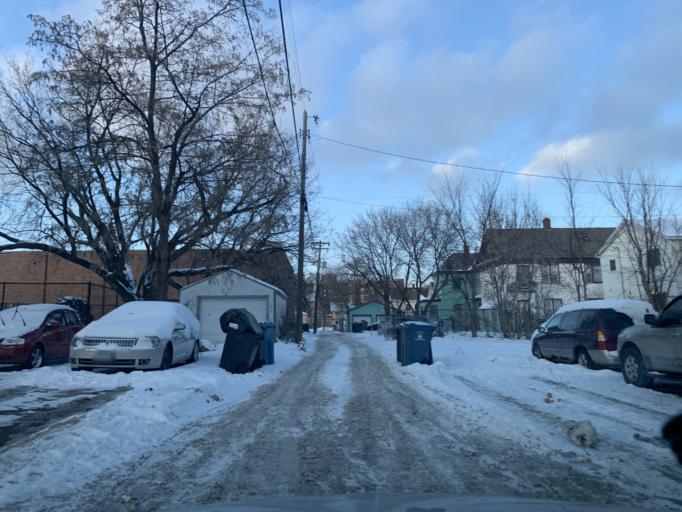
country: US
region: Minnesota
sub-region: Hennepin County
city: Minneapolis
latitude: 44.9897
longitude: -93.3026
